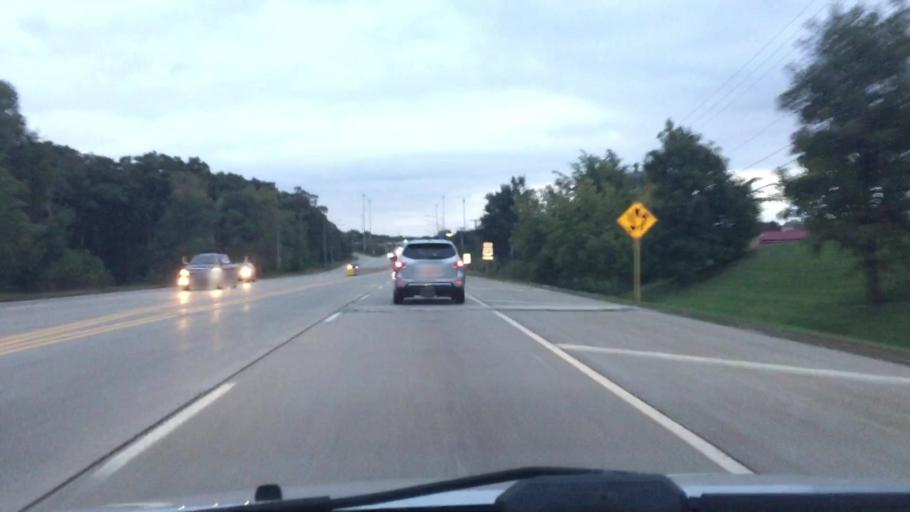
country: US
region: Illinois
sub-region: McHenry County
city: Crystal Lake
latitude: 42.2197
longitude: -88.2867
